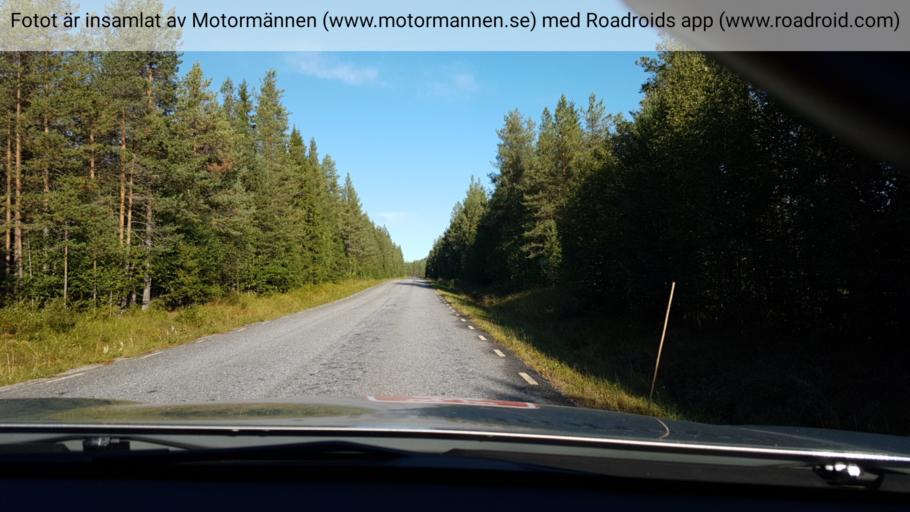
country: SE
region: Vaesterbotten
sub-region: Lycksele Kommun
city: Lycksele
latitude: 64.4766
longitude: 18.8123
